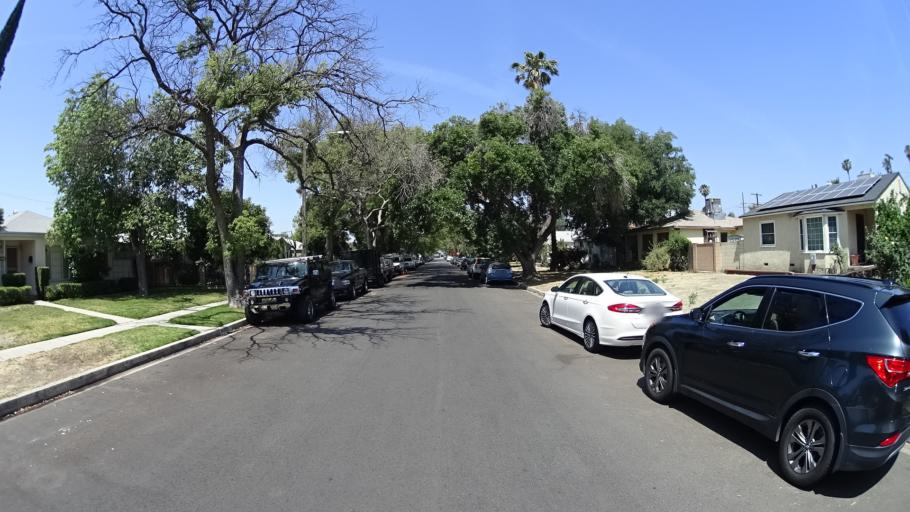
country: US
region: California
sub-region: Los Angeles County
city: Van Nuys
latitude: 34.2076
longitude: -118.4539
